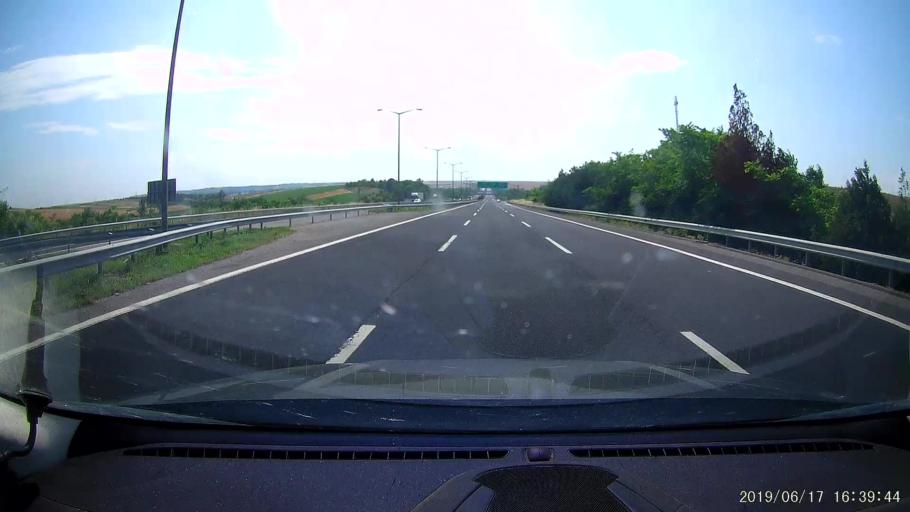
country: TR
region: Kirklareli
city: Luleburgaz
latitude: 41.4501
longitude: 27.4016
